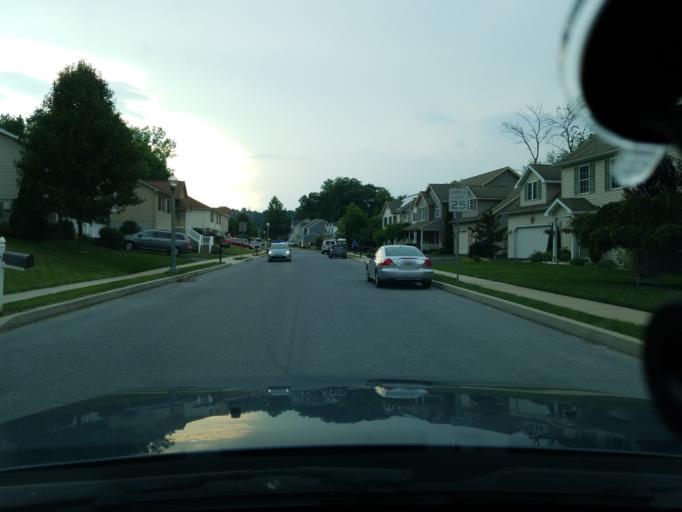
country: US
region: Pennsylvania
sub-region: Dauphin County
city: Hummelstown
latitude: 40.2704
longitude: -76.7214
